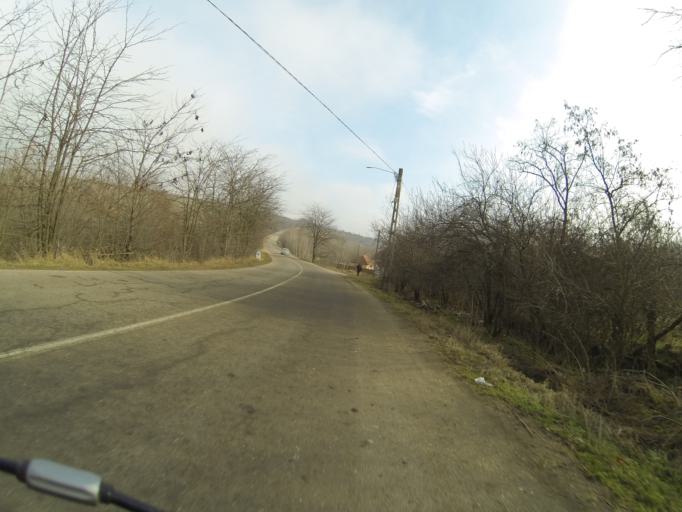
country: RO
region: Mehedinti
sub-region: Comuna Balacita
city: Balacita
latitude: 44.3855
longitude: 23.1301
